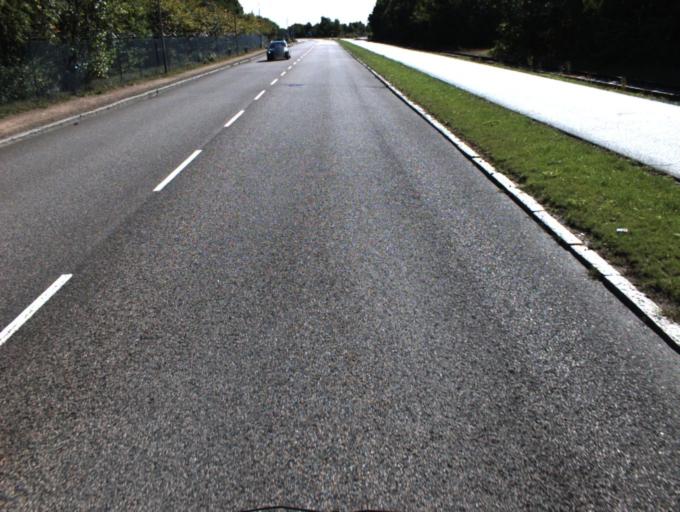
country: SE
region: Skane
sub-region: Helsingborg
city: Helsingborg
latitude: 56.0154
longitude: 12.7163
